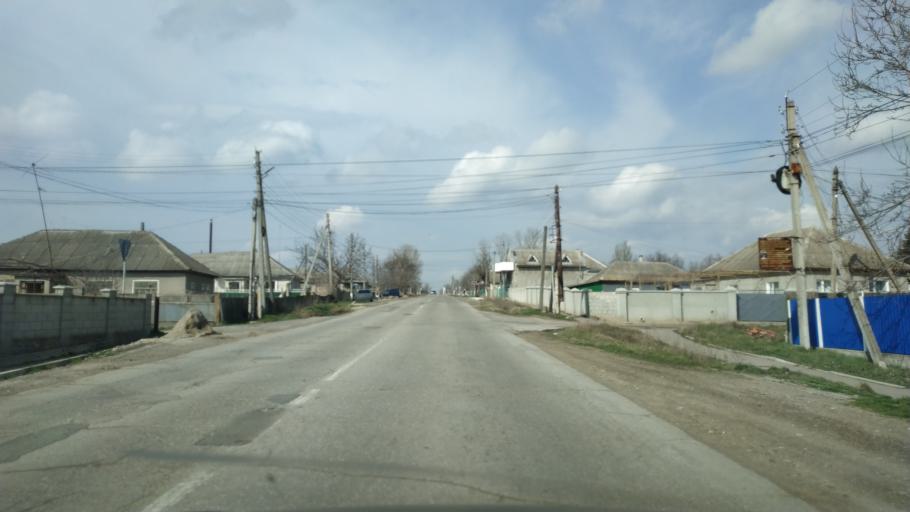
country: MD
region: Gagauzia
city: Vulcanesti
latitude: 45.6935
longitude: 28.4048
